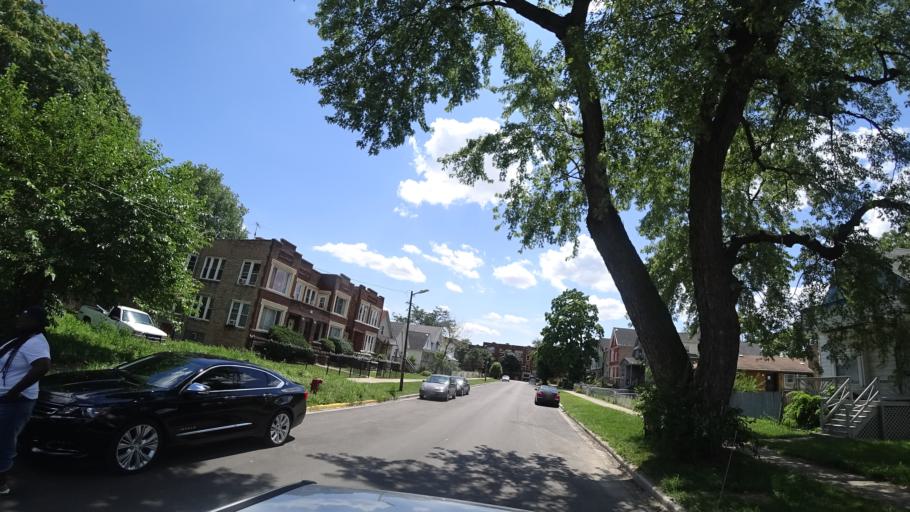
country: US
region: Illinois
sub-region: Cook County
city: Chicago
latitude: 41.7739
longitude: -87.6216
